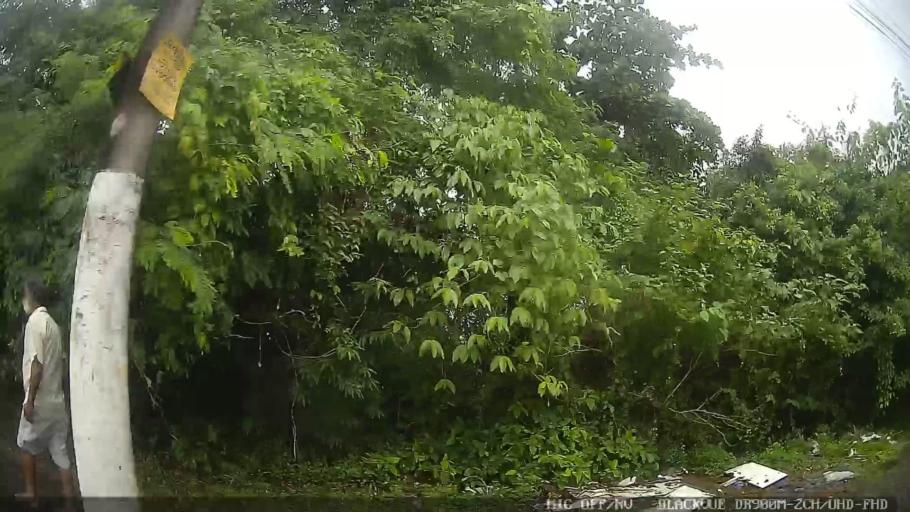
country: BR
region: Sao Paulo
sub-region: Itanhaem
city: Itanhaem
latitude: -24.1857
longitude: -46.8169
